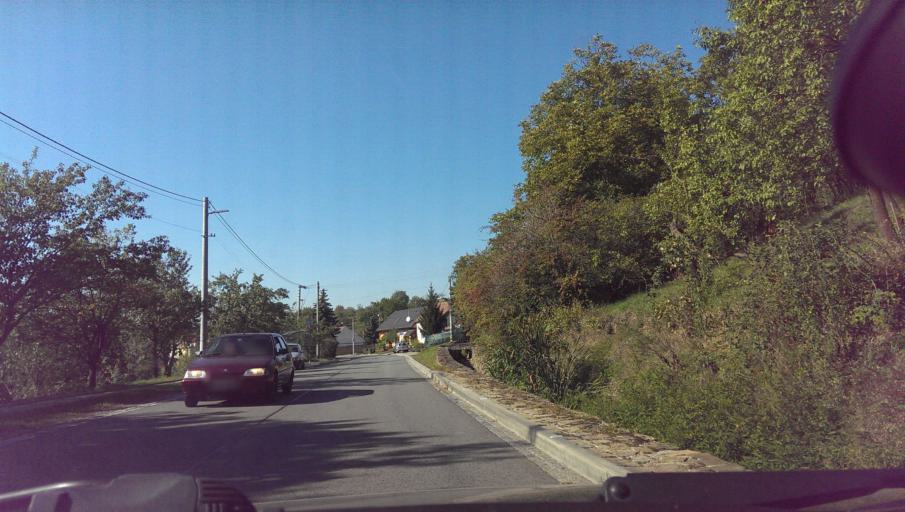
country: CZ
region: Zlin
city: Popovice
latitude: 49.0474
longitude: 17.5258
